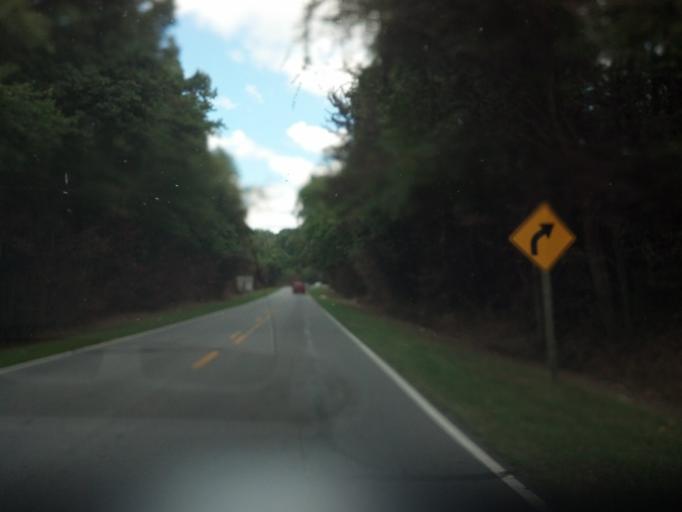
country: US
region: North Carolina
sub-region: Pitt County
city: Ayden
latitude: 35.4898
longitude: -77.4167
